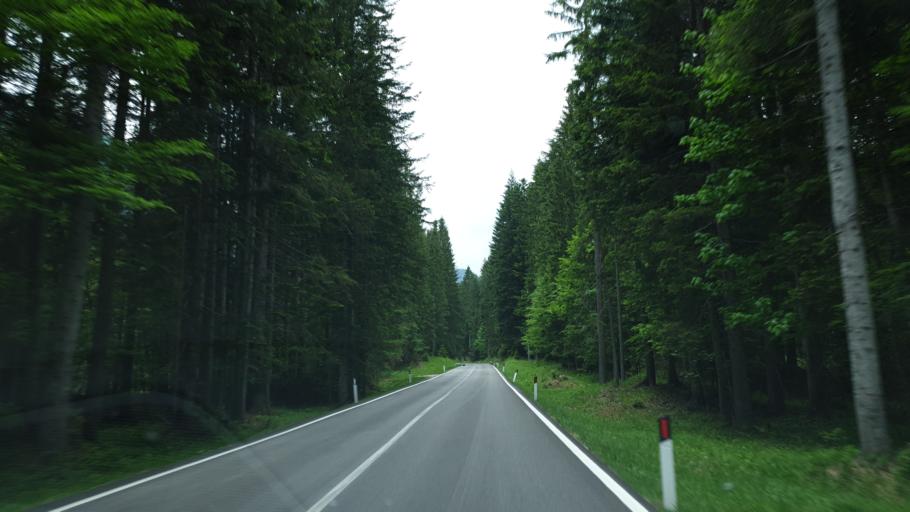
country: IT
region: Veneto
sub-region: Provincia di Belluno
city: San Vito
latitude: 46.5313
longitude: 12.2791
